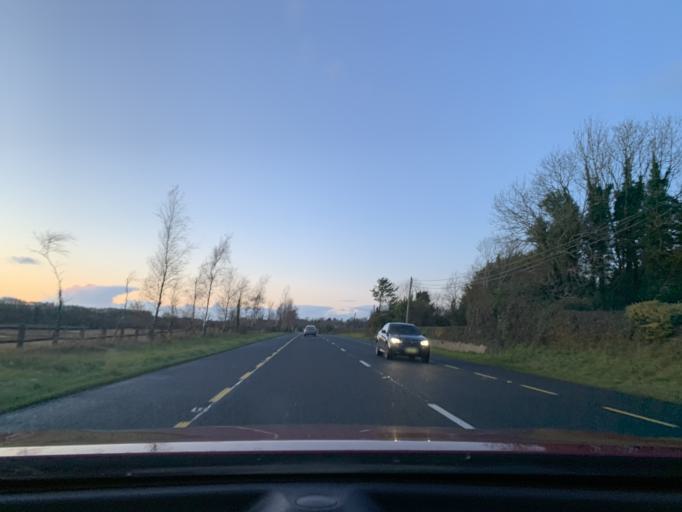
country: IE
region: Connaught
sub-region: County Leitrim
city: Carrick-on-Shannon
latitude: 53.9147
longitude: -7.9725
